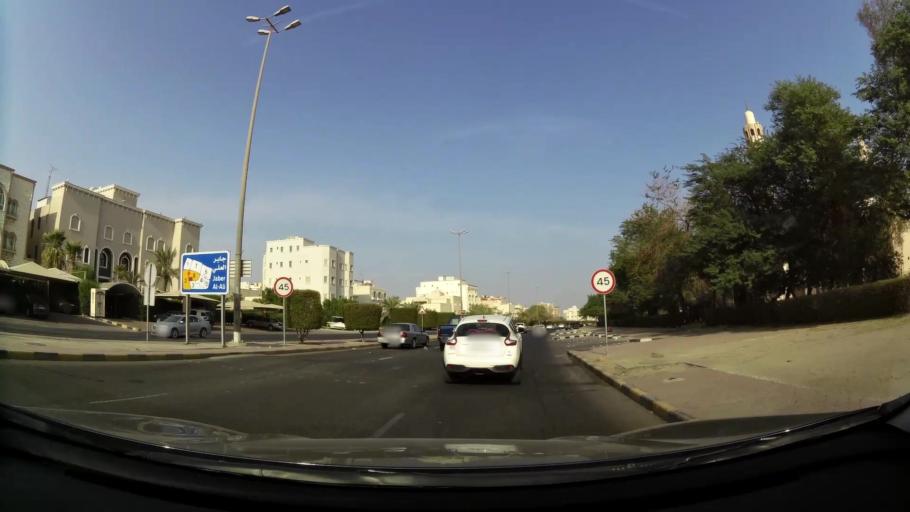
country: KW
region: Mubarak al Kabir
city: Mubarak al Kabir
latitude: 29.1735
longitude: 48.0775
